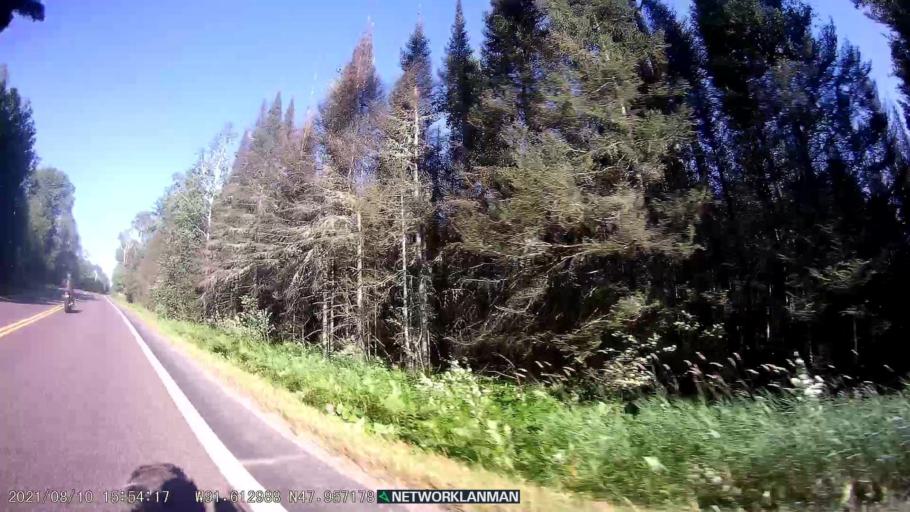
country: US
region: Minnesota
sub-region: Saint Louis County
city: Ely
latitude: 47.9572
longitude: -91.6128
